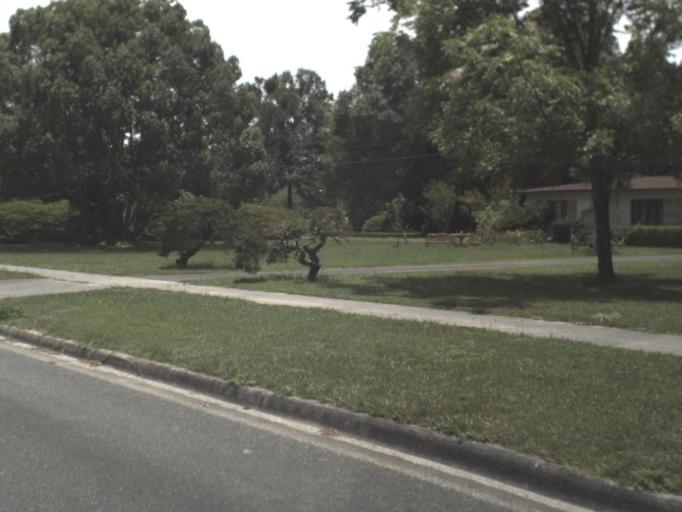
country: US
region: Florida
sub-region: Bradford County
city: Starke
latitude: 29.9608
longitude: -82.1172
